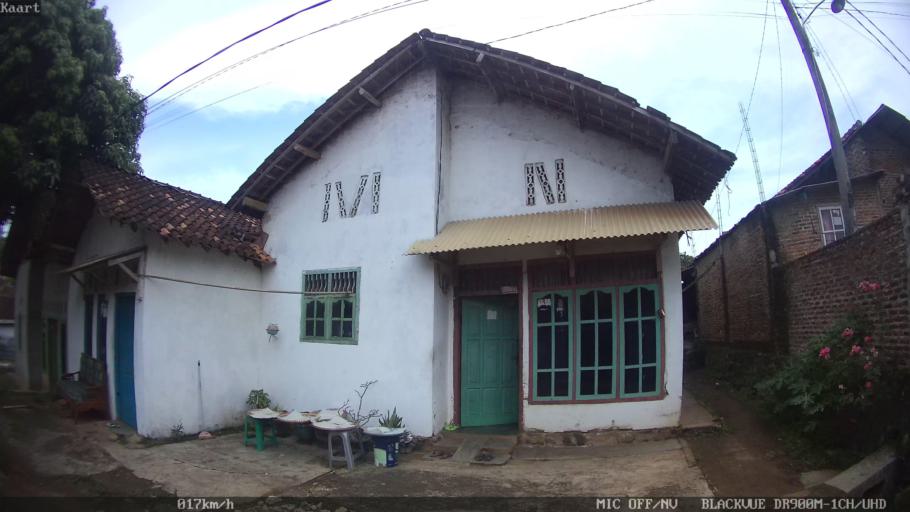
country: ID
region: Lampung
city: Kedaton
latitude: -5.3901
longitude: 105.1976
